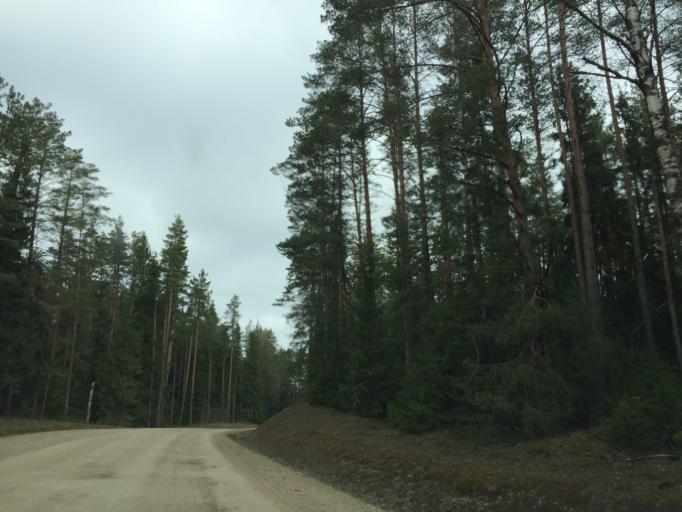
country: EE
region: Valgamaa
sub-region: Valga linn
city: Valga
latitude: 57.5929
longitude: 26.2204
